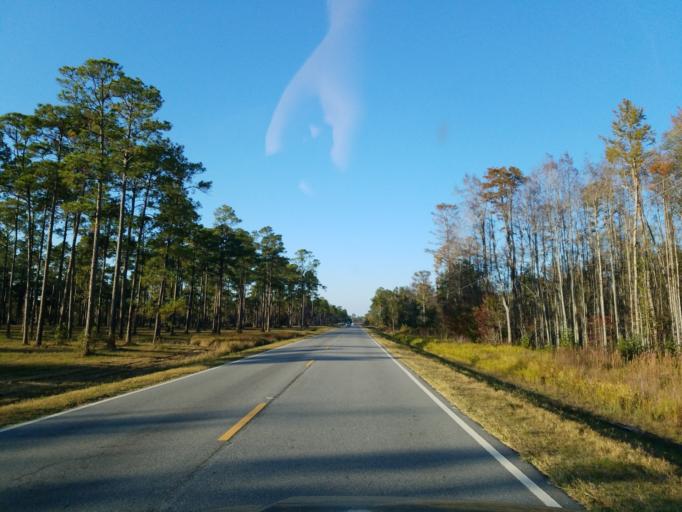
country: US
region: Georgia
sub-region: Lanier County
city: Lakeland
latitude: 31.1191
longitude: -83.0833
